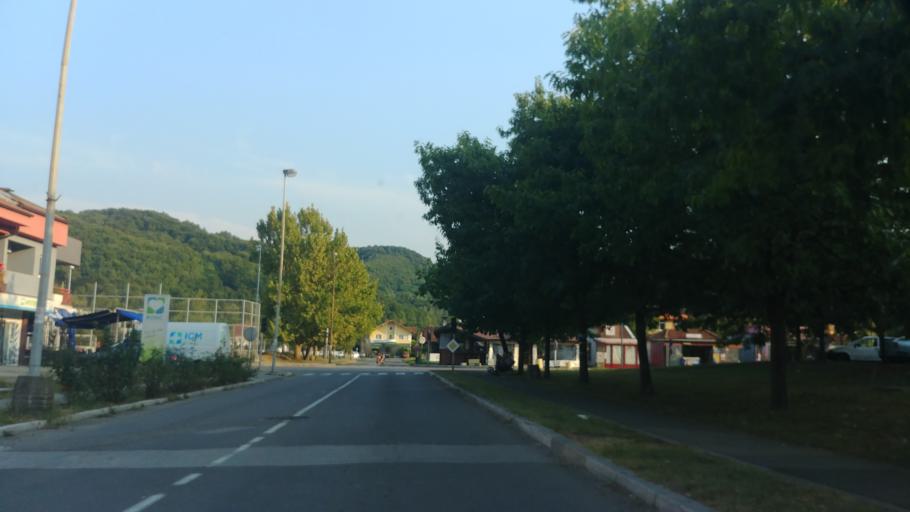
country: BA
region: Republika Srpska
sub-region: Opstina Ugljevik
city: Ugljevik
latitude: 44.6927
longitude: 18.9950
